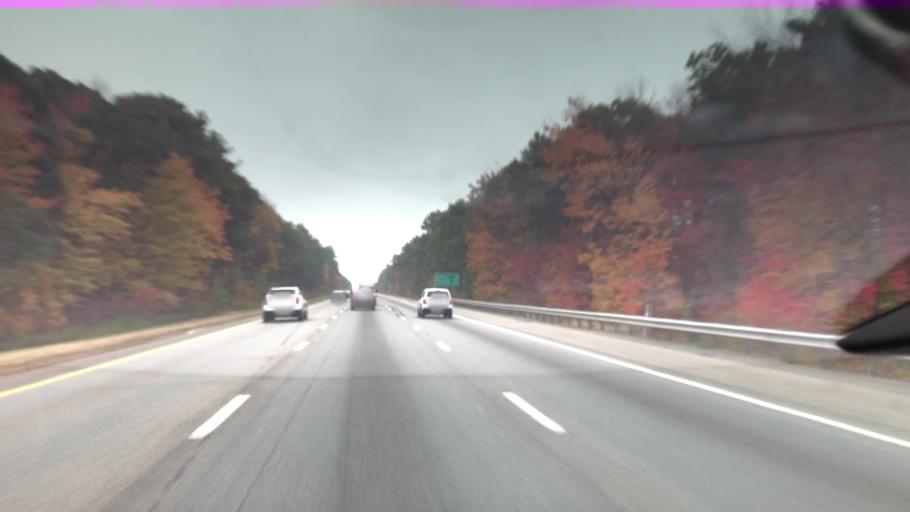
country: US
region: Massachusetts
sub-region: Middlesex County
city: Littleton Common
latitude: 42.5102
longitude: -71.5209
